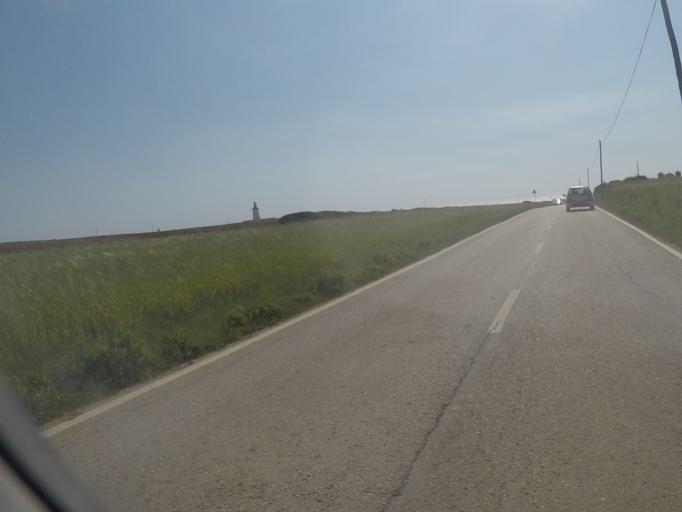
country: PT
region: Setubal
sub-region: Sesimbra
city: Sesimbra
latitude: 38.4201
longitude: -9.2091
